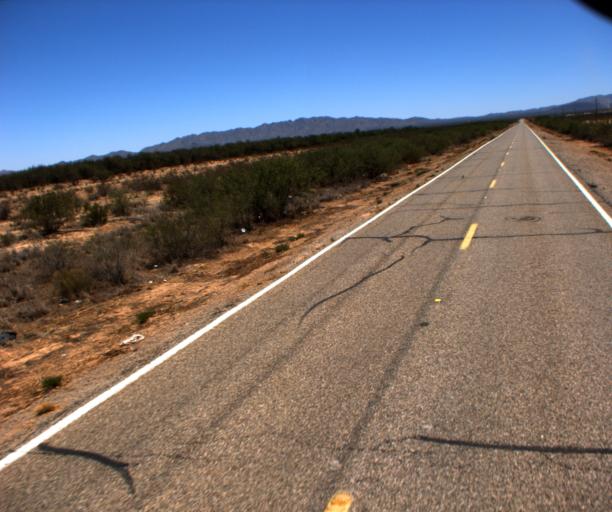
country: US
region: Arizona
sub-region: Pima County
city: Ajo
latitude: 32.1873
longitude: -112.3869
